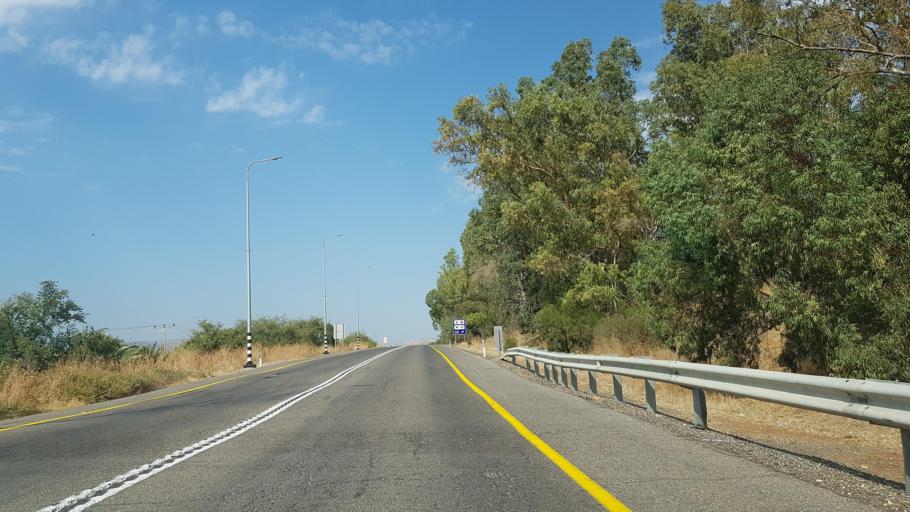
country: SY
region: Quneitra
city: Al Butayhah
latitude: 32.8499
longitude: 35.6526
